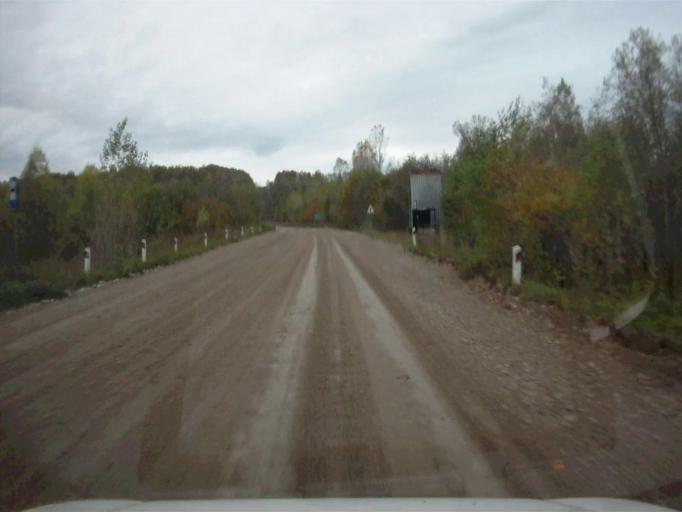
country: RU
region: Chelyabinsk
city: Nyazepetrovsk
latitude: 56.1331
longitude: 59.3157
